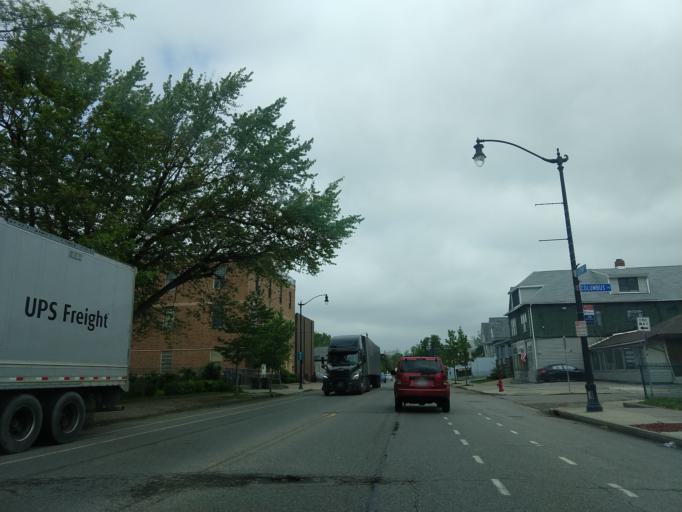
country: US
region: New York
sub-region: Erie County
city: Lackawanna
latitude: 42.8475
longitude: -78.8237
